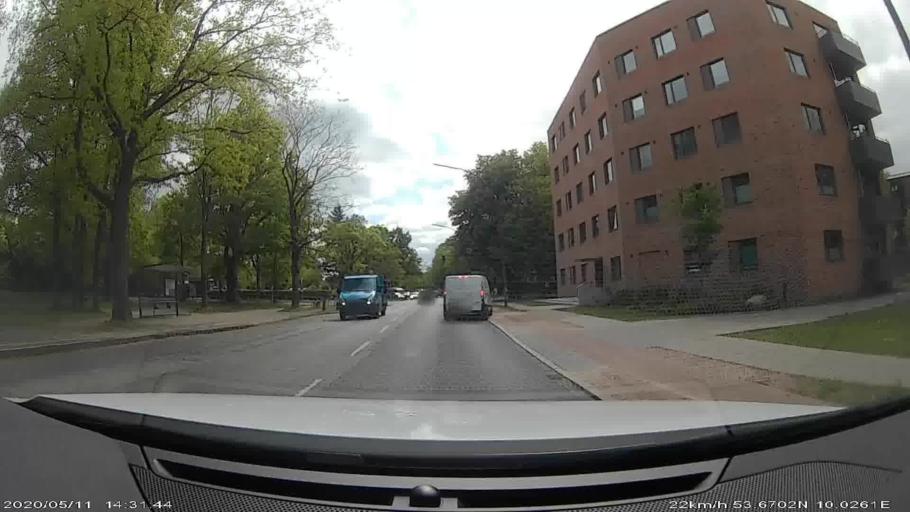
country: DE
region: Hamburg
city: Langenhorn
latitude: 53.6609
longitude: 10.0217
